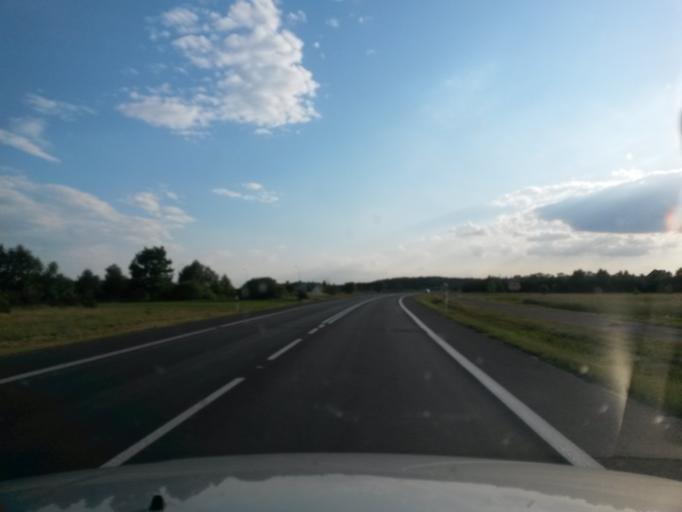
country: PL
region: Lodz Voivodeship
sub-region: Powiat belchatowski
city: Szczercow
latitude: 51.3408
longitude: 19.0802
